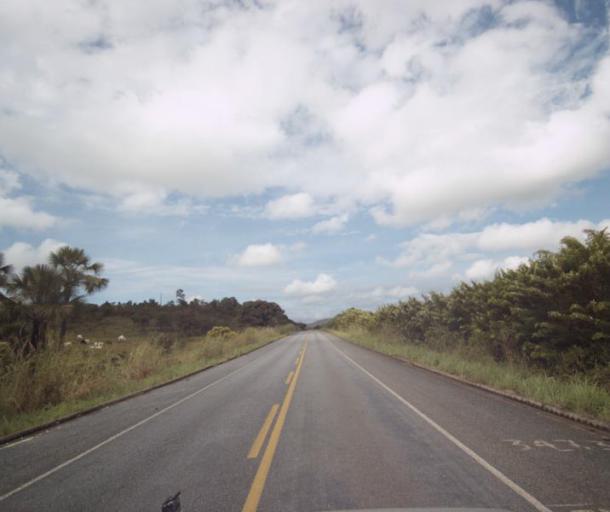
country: BR
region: Goias
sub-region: Pirenopolis
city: Pirenopolis
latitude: -15.6157
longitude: -48.6603
